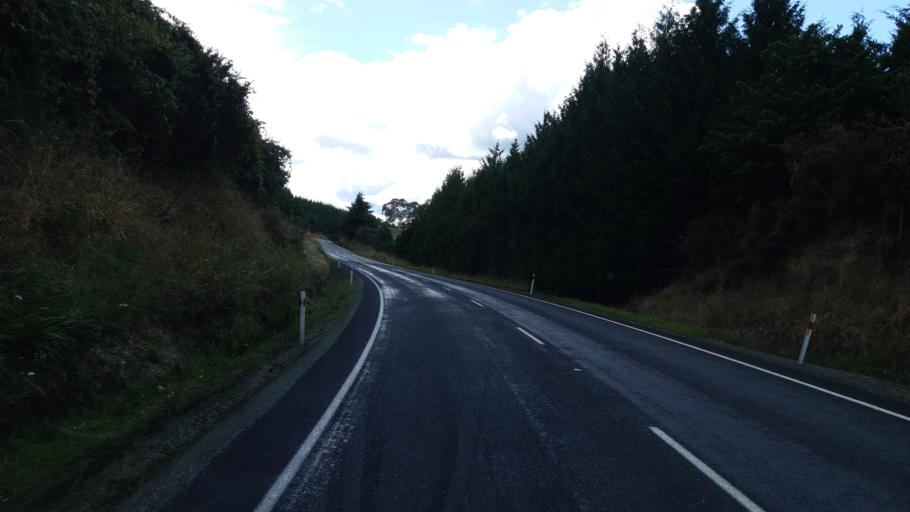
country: NZ
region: Tasman
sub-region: Tasman District
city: Wakefield
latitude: -41.5540
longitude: 172.7890
